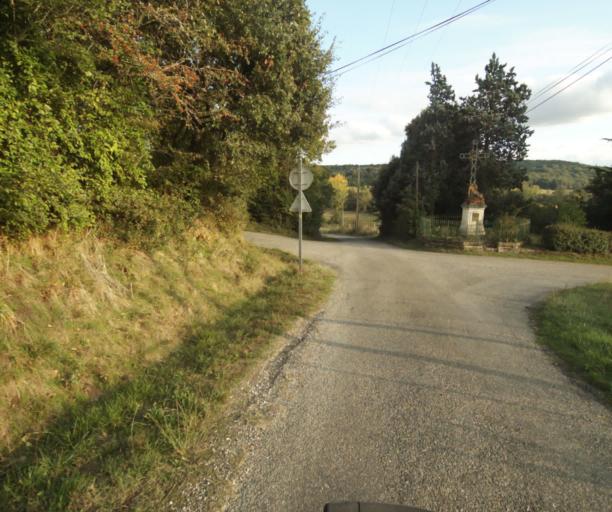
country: FR
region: Midi-Pyrenees
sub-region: Departement de la Haute-Garonne
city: Launac
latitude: 43.8198
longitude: 1.1210
